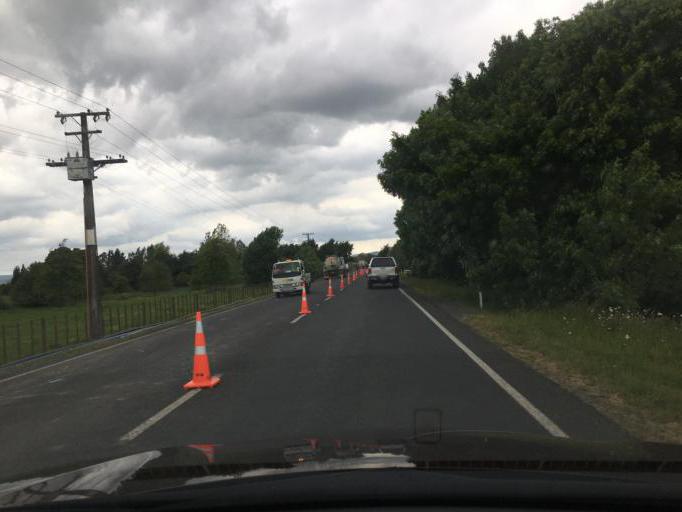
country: NZ
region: Waikato
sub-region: Waipa District
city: Cambridge
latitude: -37.9180
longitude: 175.4409
